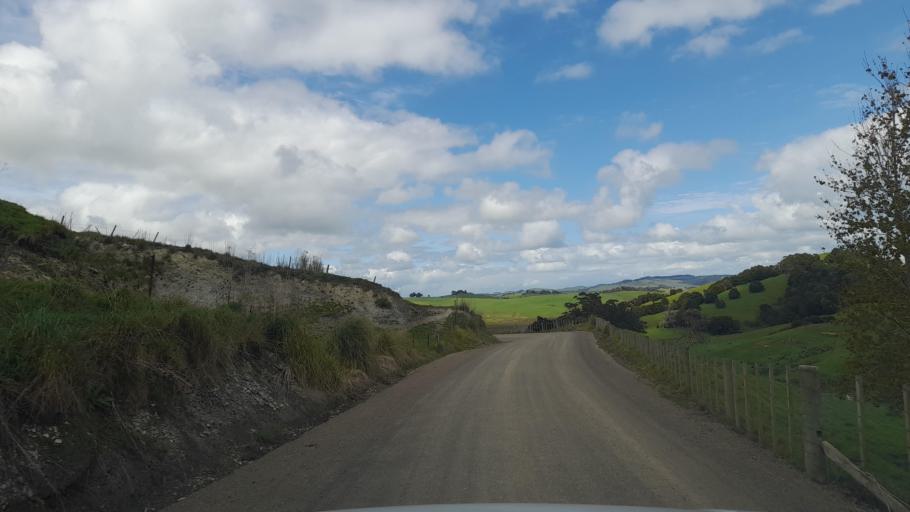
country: NZ
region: Auckland
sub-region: Auckland
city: Wellsford
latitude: -36.1861
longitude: 174.3221
